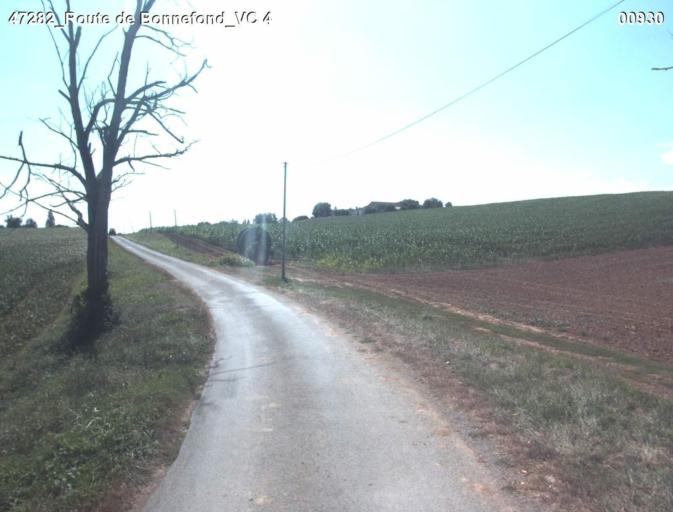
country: FR
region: Aquitaine
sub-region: Departement du Lot-et-Garonne
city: Laplume
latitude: 44.1125
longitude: 0.4766
